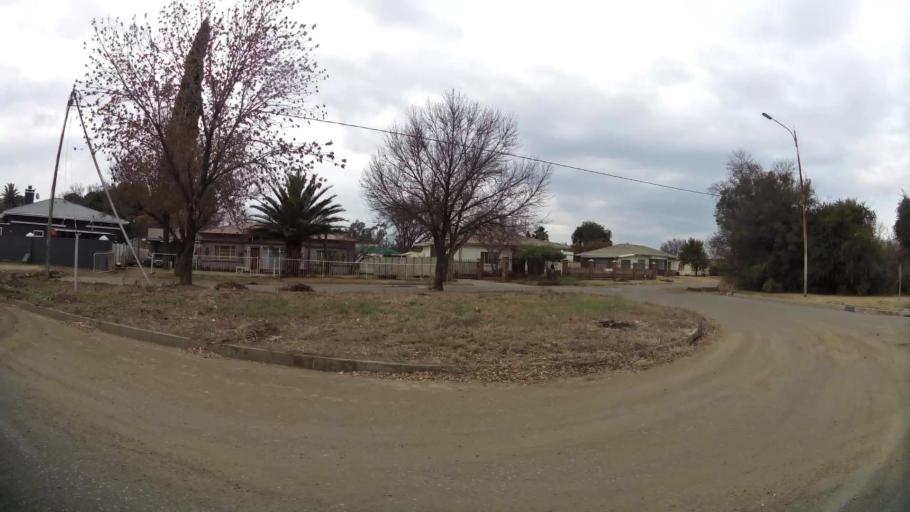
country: ZA
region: Orange Free State
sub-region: Fezile Dabi District Municipality
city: Kroonstad
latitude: -27.6724
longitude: 27.2300
